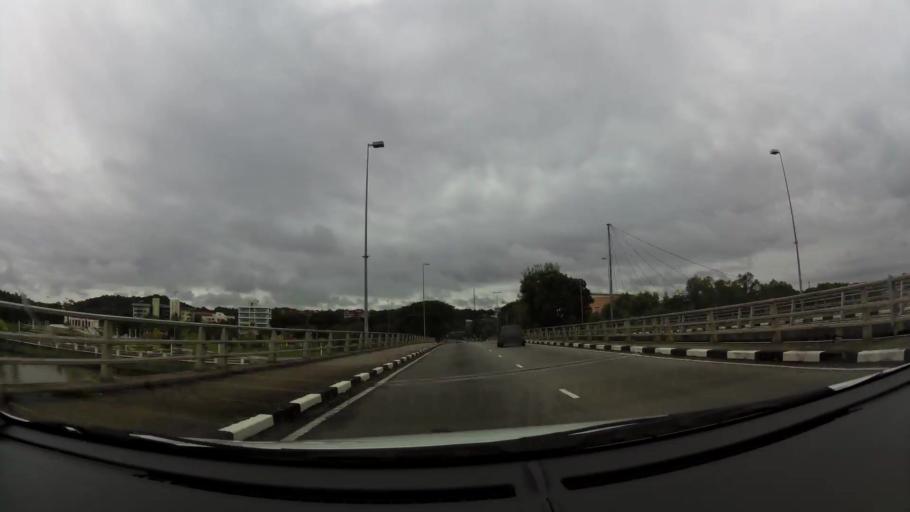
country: BN
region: Brunei and Muara
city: Bandar Seri Begawan
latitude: 4.8978
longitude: 114.9336
